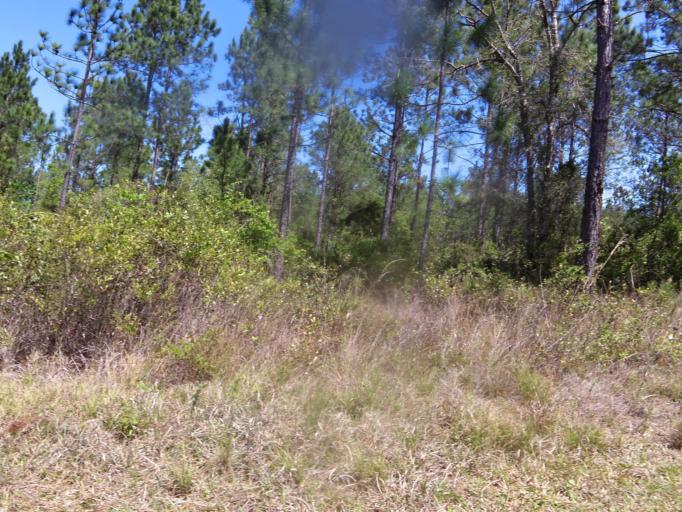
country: US
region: Florida
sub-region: Putnam County
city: Palatka
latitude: 29.6831
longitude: -81.7384
